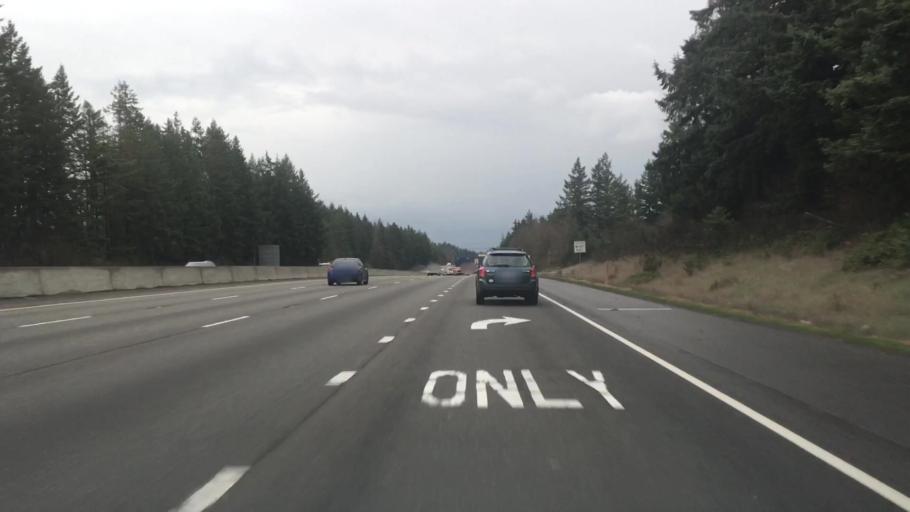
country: US
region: Washington
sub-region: Thurston County
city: Grand Mound
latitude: 46.8795
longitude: -122.9666
